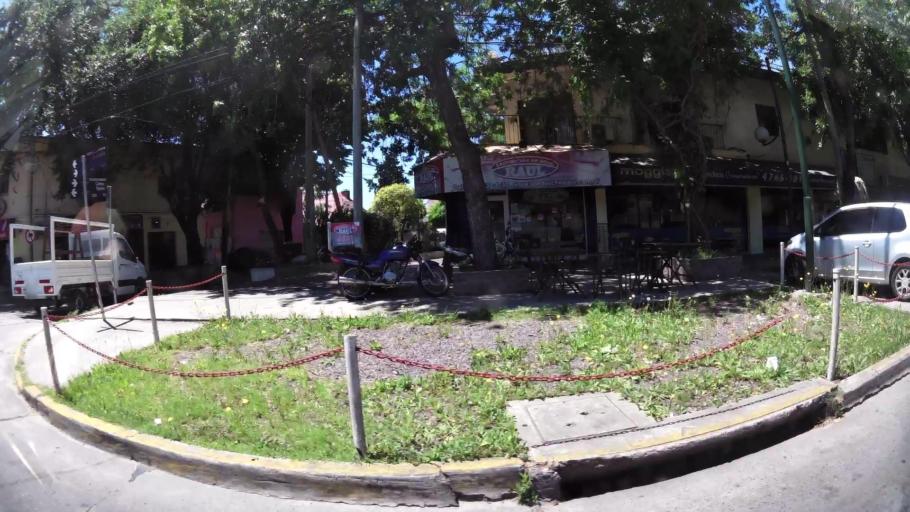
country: AR
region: Buenos Aires
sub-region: Partido de San Isidro
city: San Isidro
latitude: -34.4977
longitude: -58.5595
